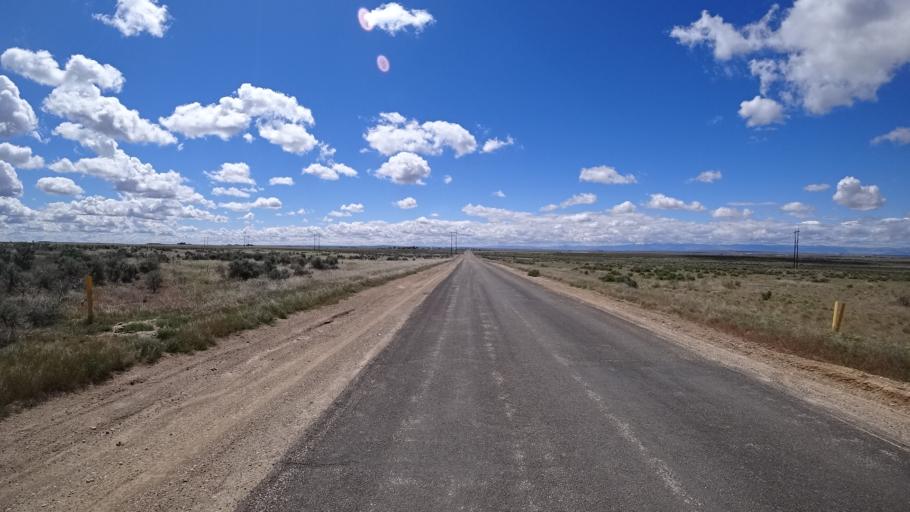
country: US
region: Idaho
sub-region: Ada County
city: Kuna
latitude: 43.4795
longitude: -116.2743
